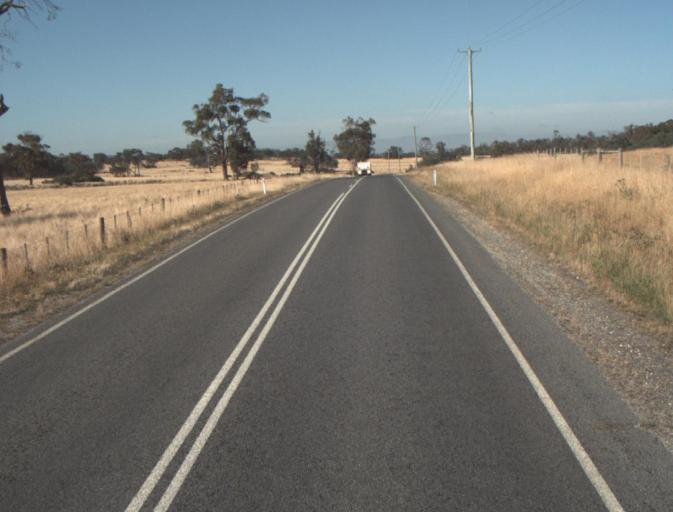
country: AU
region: Tasmania
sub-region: Launceston
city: Newstead
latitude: -41.4424
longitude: 147.2540
